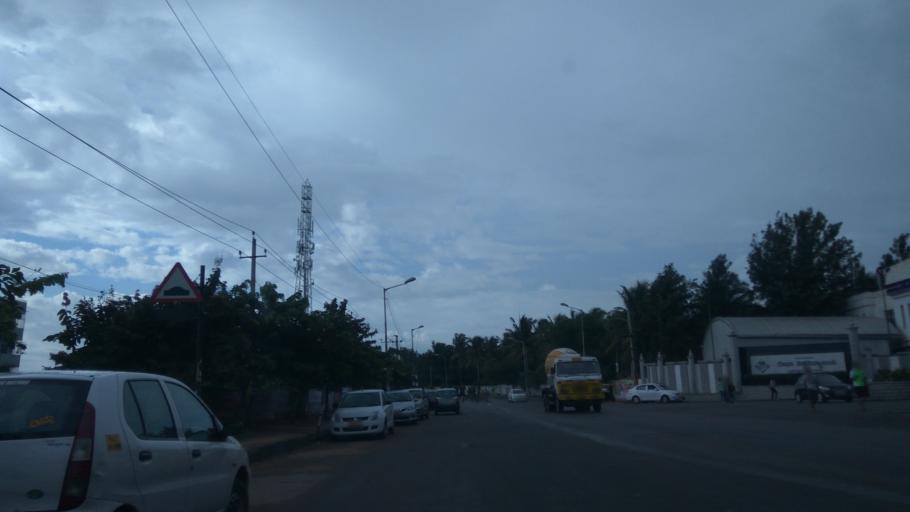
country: IN
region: Karnataka
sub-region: Bangalore Urban
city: Yelahanka
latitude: 13.1169
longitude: 77.6341
